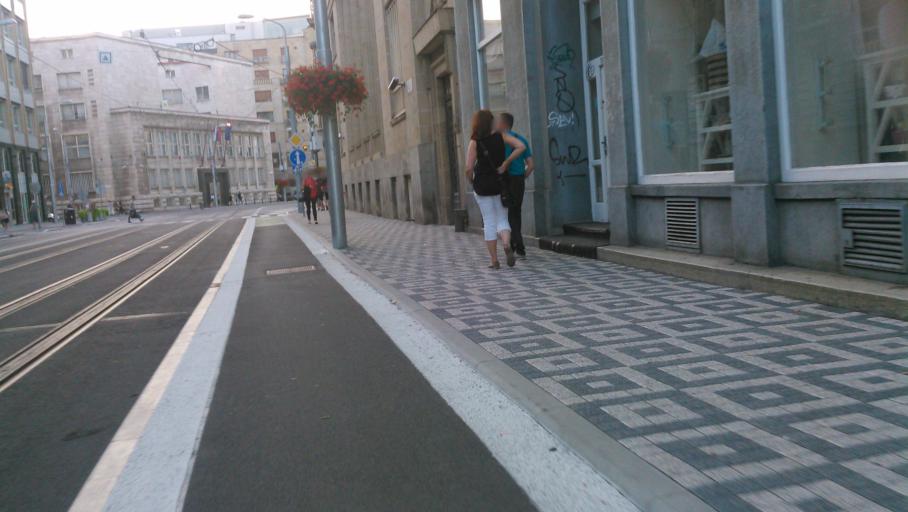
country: SK
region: Bratislavsky
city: Bratislava
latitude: 48.1429
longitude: 17.1140
